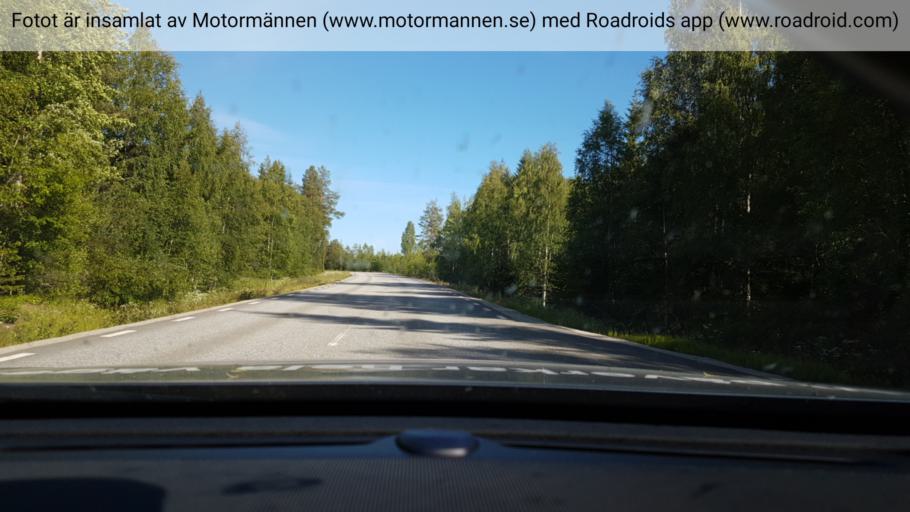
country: SE
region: Vaesterbotten
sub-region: Lycksele Kommun
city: Lycksele
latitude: 64.6502
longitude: 18.4657
